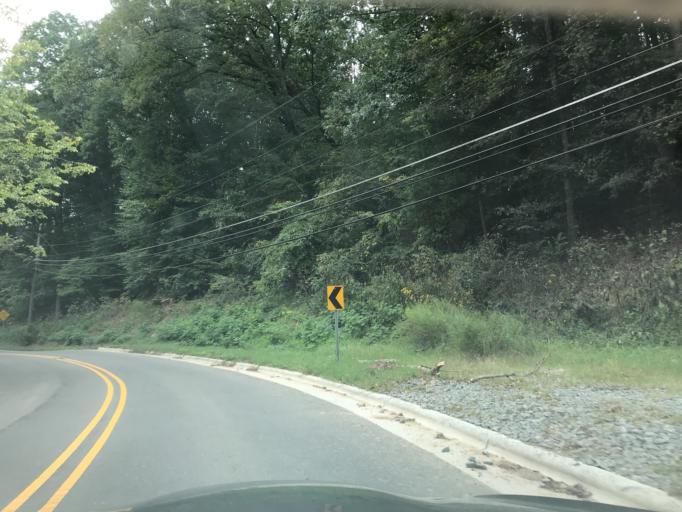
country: US
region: North Carolina
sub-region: Orange County
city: Chapel Hill
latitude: 35.9254
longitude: -79.0558
